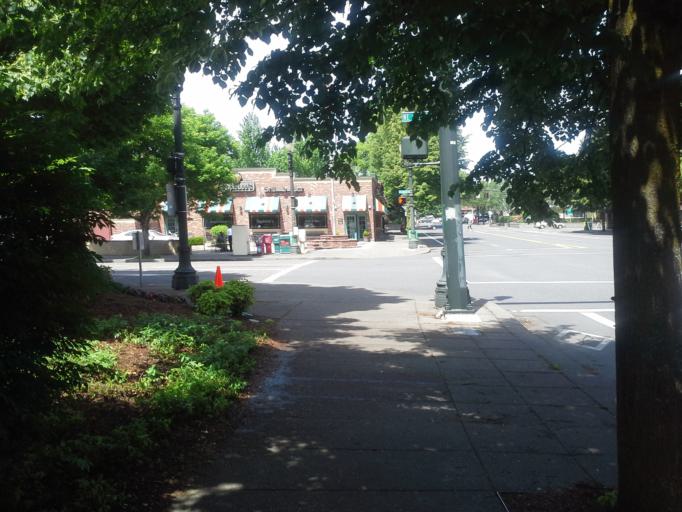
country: US
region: Oregon
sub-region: Multnomah County
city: Portland
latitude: 45.5334
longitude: -122.6506
